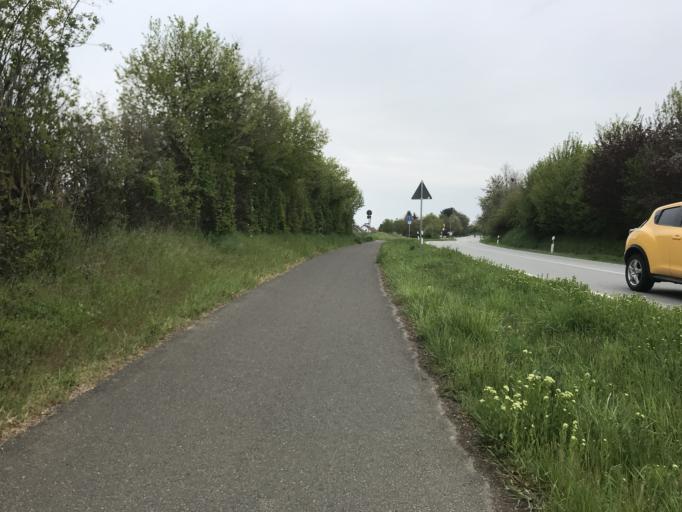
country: DE
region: Rheinland-Pfalz
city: Appenheim
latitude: 49.9363
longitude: 8.0281
